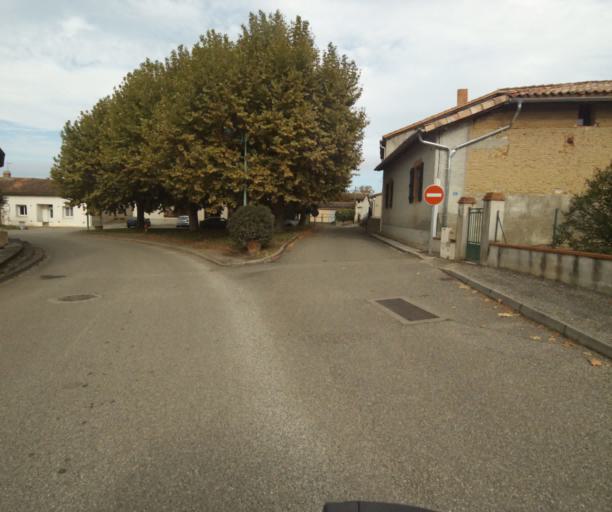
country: FR
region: Midi-Pyrenees
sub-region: Departement du Tarn-et-Garonne
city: Finhan
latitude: 43.9146
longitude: 1.2184
